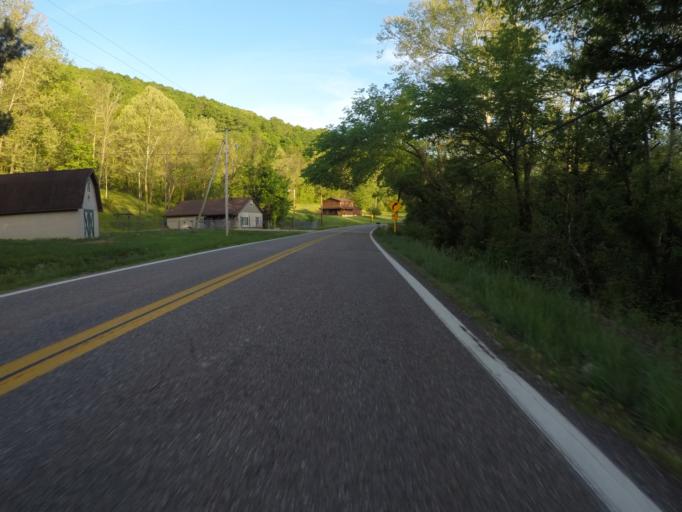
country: US
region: West Virginia
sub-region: Cabell County
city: Huntington
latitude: 38.5012
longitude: -82.4757
